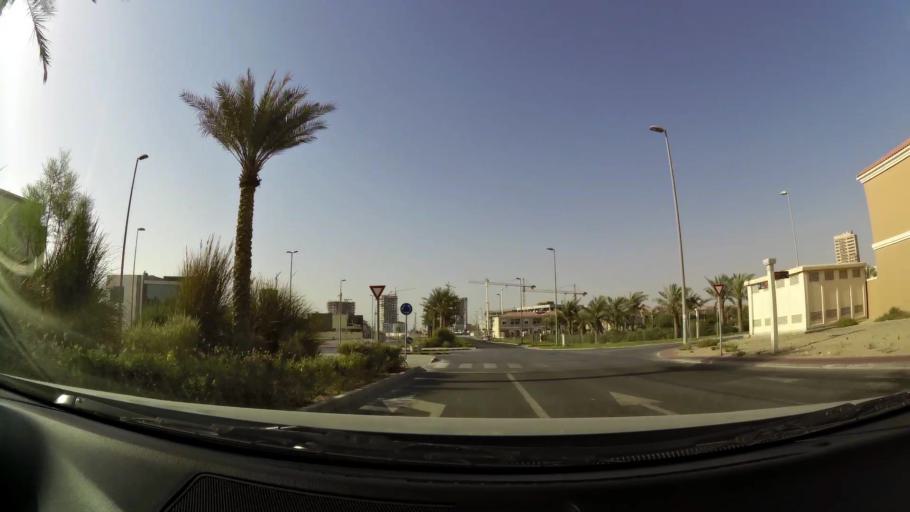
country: AE
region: Dubai
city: Dubai
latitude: 25.0544
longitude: 55.2156
